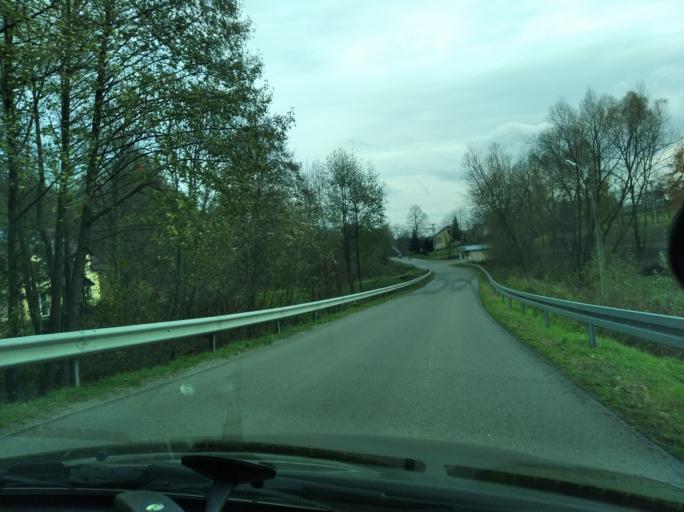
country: PL
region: Subcarpathian Voivodeship
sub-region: Powiat ropczycko-sedziszowski
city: Zagorzyce
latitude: 49.9545
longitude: 21.7210
